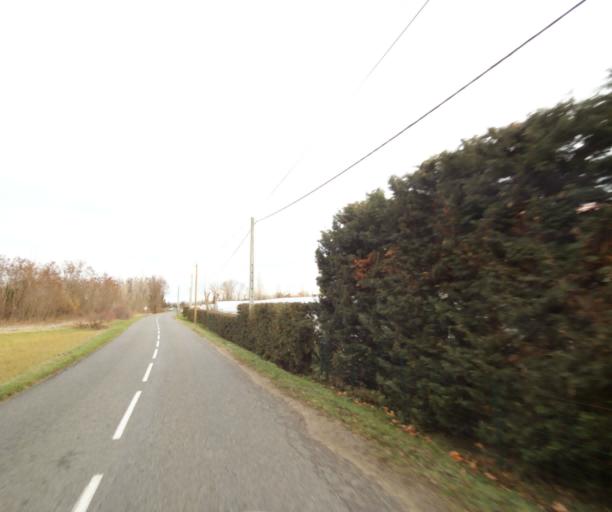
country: FR
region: Rhone-Alpes
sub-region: Departement de la Loire
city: Saint-Marcellin-en-Forez
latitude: 45.5136
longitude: 4.1791
